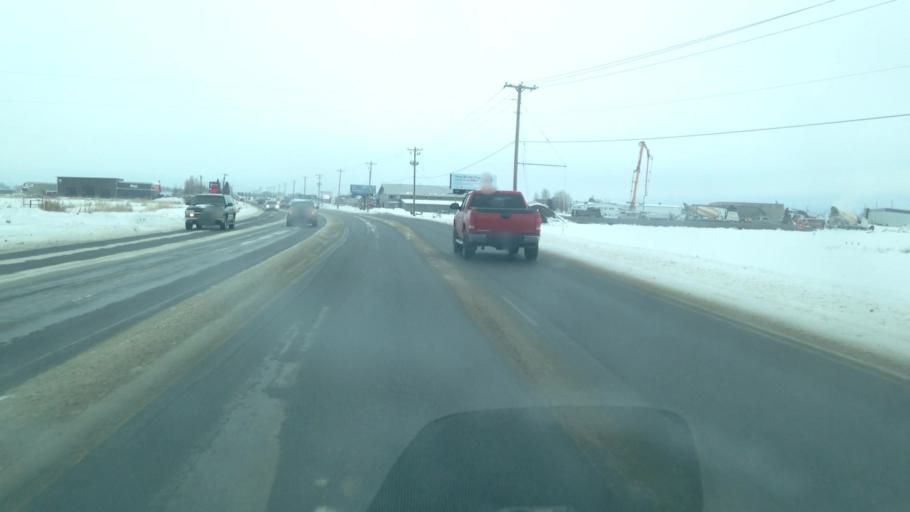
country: US
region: Idaho
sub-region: Madison County
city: Rexburg
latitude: 43.8442
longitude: -111.7782
